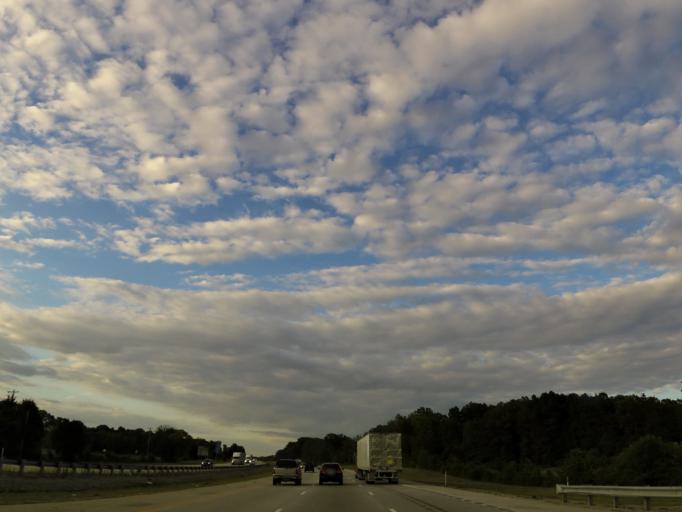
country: US
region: Tennessee
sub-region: Hamilton County
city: Collegedale
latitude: 35.0932
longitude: -85.0575
